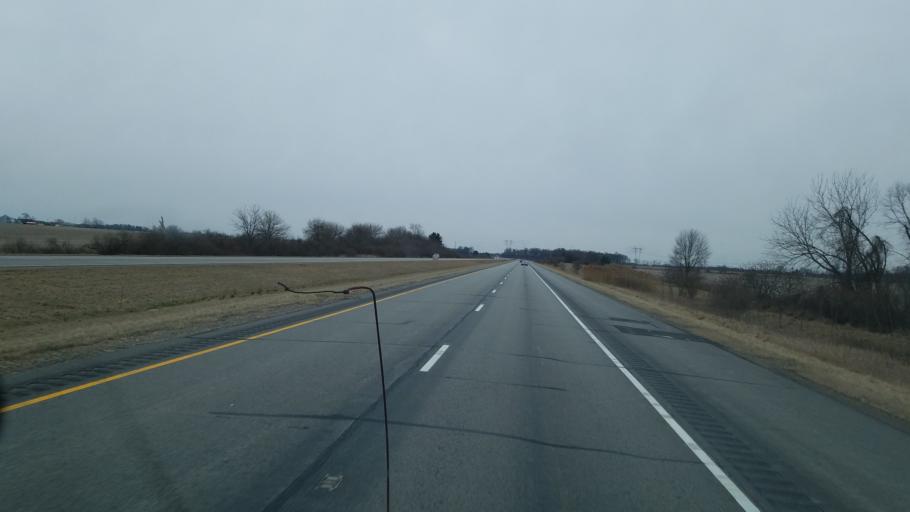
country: US
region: Indiana
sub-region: Marshall County
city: Argos
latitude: 41.2243
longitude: -86.2613
